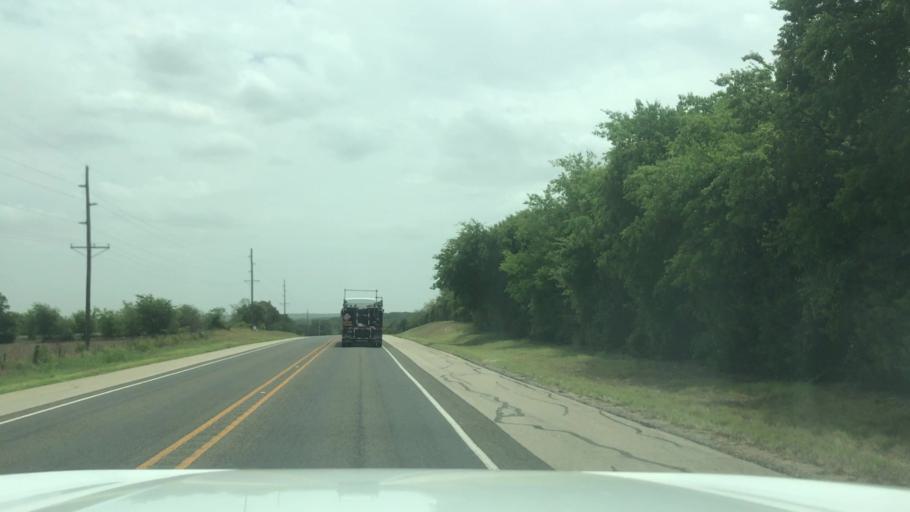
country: US
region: Texas
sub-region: Bosque County
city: Valley Mills
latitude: 31.6868
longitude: -97.5301
